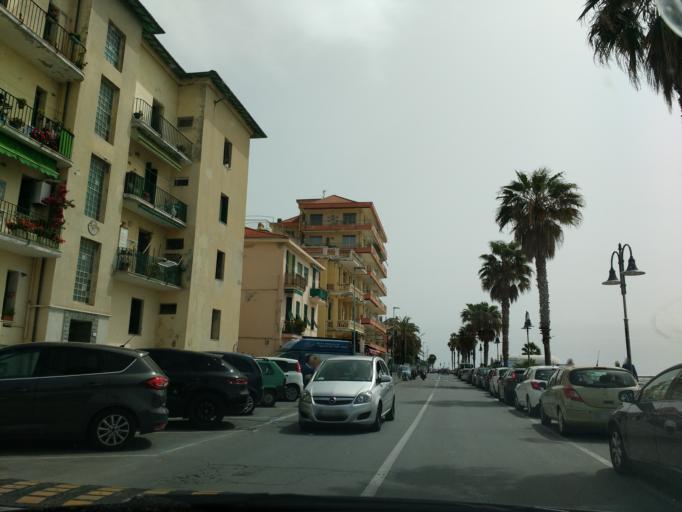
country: IT
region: Liguria
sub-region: Provincia di Imperia
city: Ventimiglia
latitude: 43.7872
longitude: 7.6126
